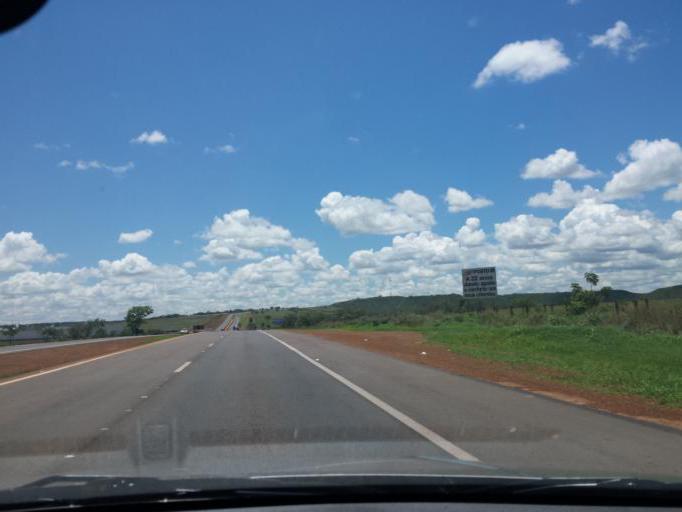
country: BR
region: Goias
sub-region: Cristalina
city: Cristalina
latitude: -16.6173
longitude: -47.7542
